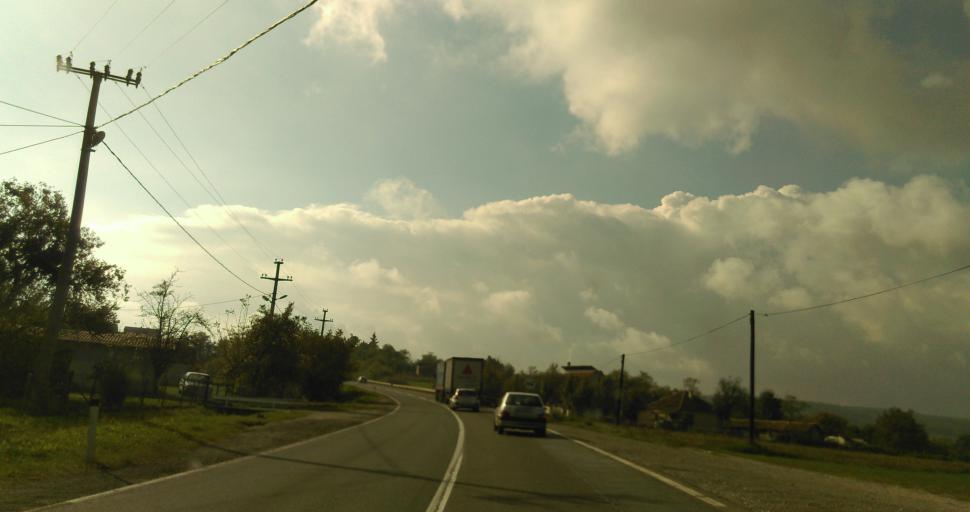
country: RS
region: Central Serbia
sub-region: Kolubarski Okrug
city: Lajkovac
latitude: 44.3582
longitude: 20.1897
